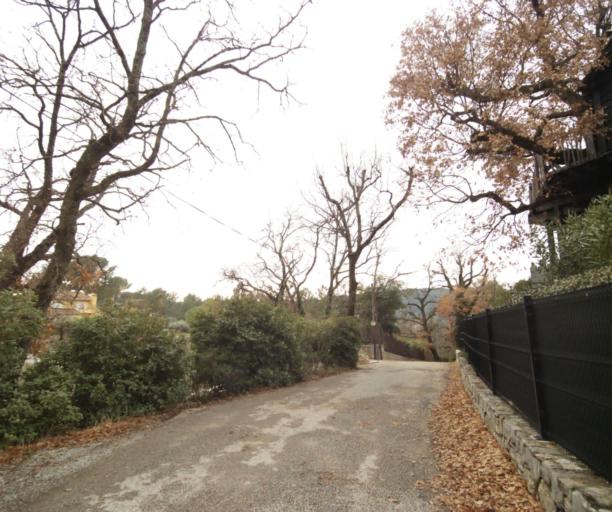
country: FR
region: Provence-Alpes-Cote d'Azur
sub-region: Departement du Var
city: Trans-en-Provence
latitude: 43.5155
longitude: 6.4818
